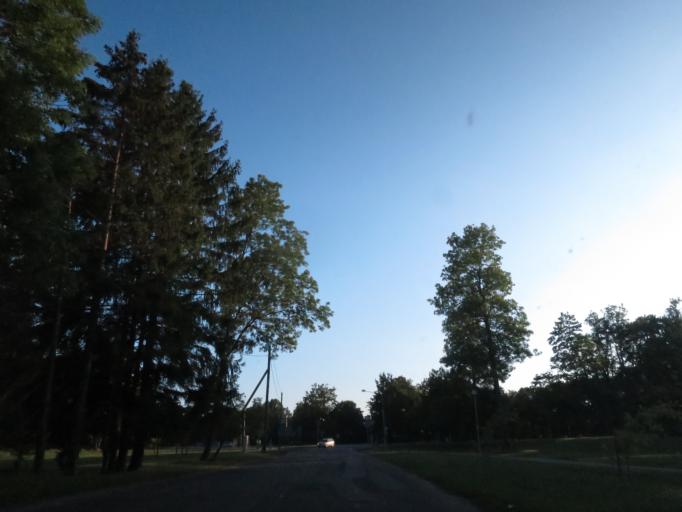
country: LV
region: Sigulda
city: Sigulda
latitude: 57.1627
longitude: 24.8565
